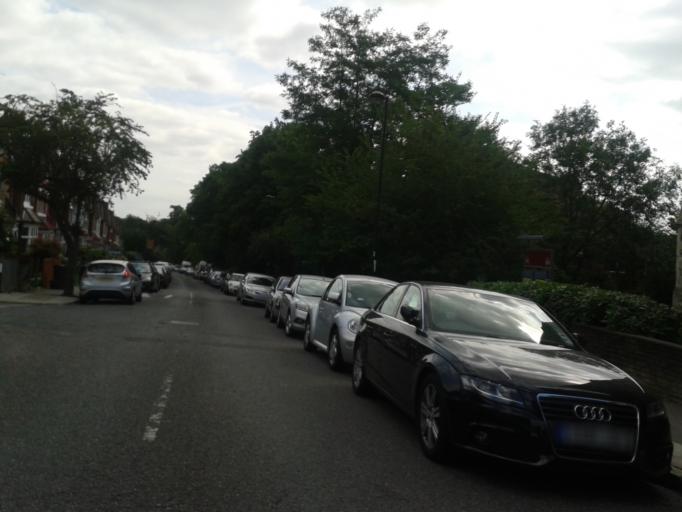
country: GB
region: England
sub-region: Greater London
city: Brixton Hill
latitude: 51.4454
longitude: -0.1095
